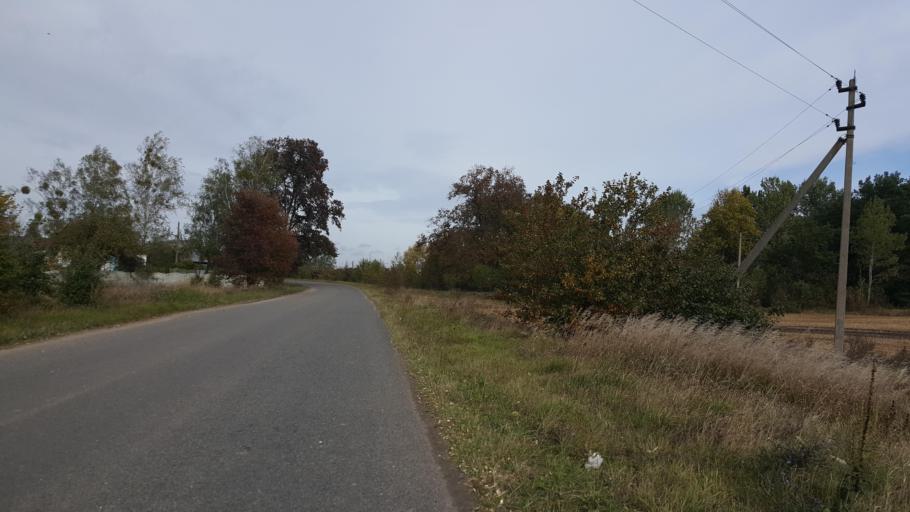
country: BY
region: Brest
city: Kamyanyets
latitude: 52.4169
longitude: 23.8880
